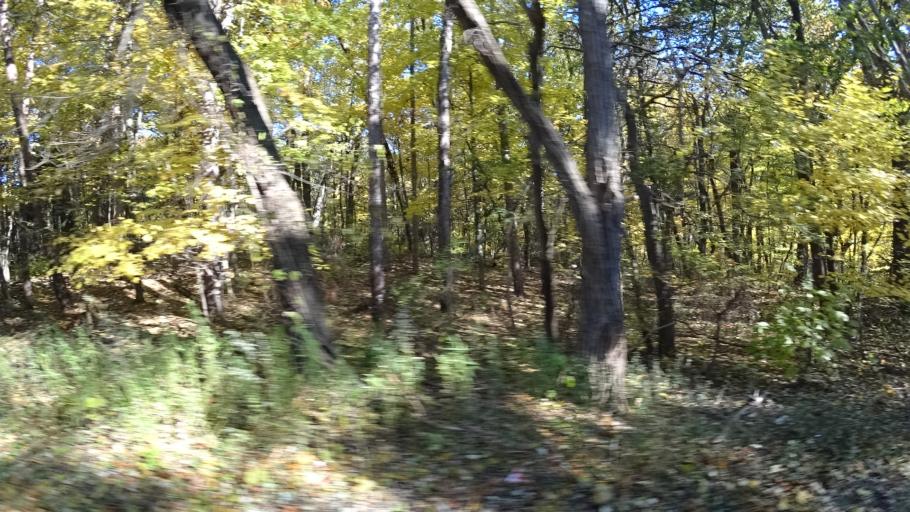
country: US
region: Indiana
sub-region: LaPorte County
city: Michigan City
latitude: 41.7178
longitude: -86.8735
